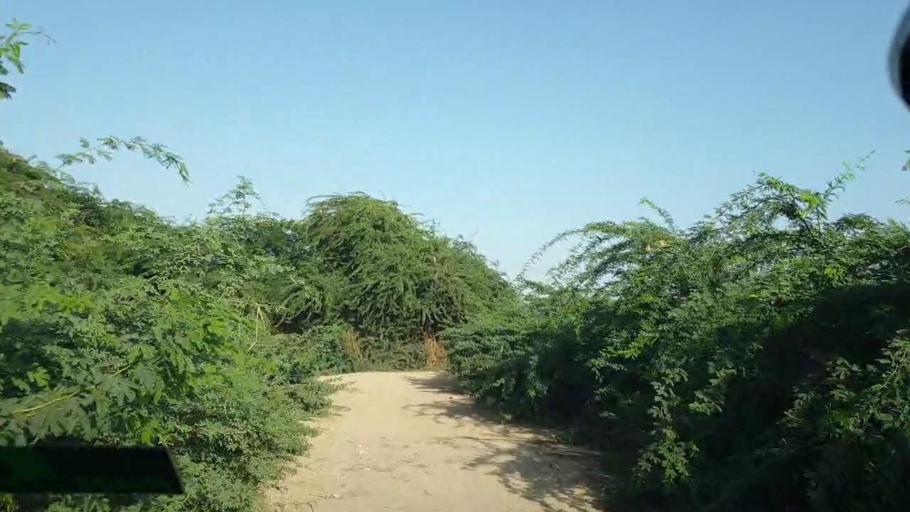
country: PK
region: Sindh
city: Naukot
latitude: 24.7319
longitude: 69.2574
